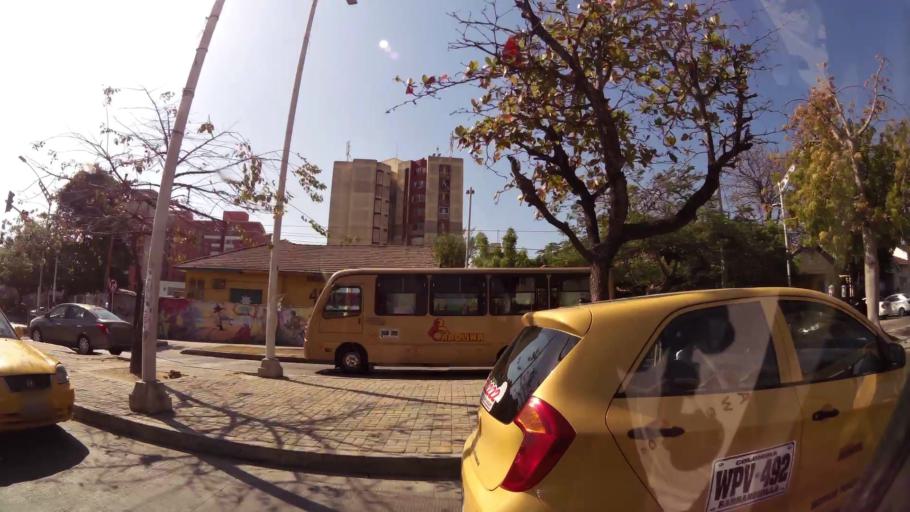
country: CO
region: Atlantico
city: Barranquilla
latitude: 10.9928
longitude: -74.7895
